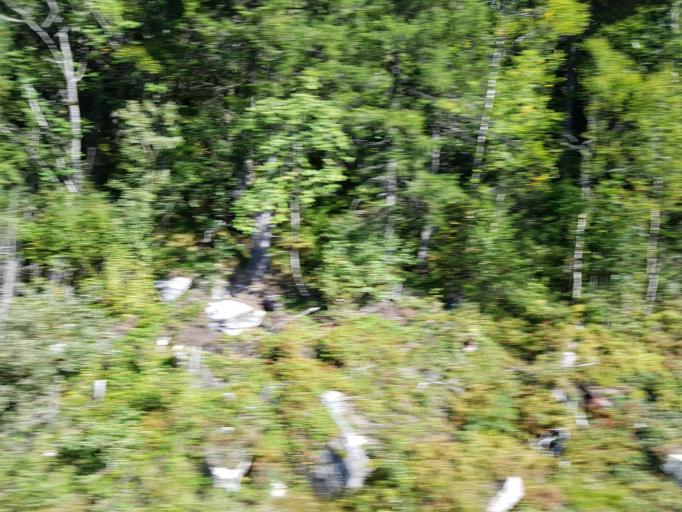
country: NO
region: Sor-Trondelag
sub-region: Afjord
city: A i Afjord
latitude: 63.7400
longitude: 10.2364
